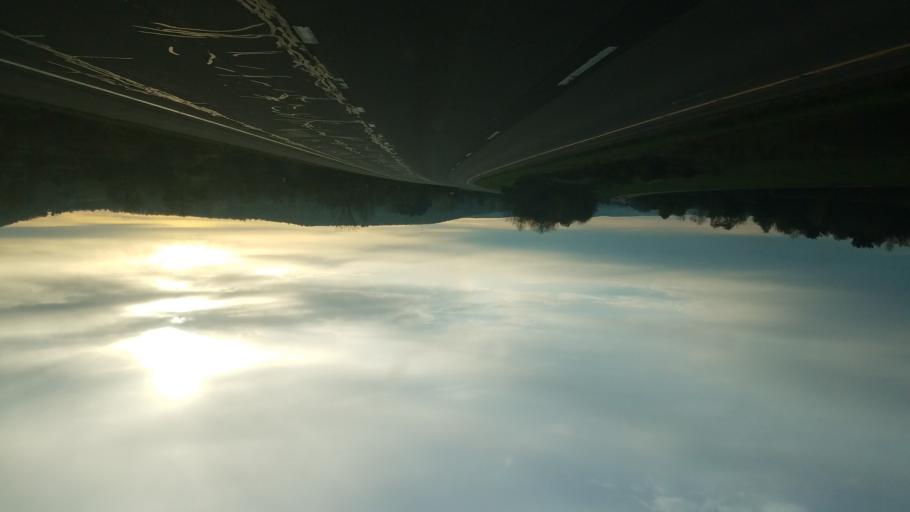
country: US
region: New York
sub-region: Allegany County
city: Friendship
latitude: 42.2260
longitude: -78.0975
